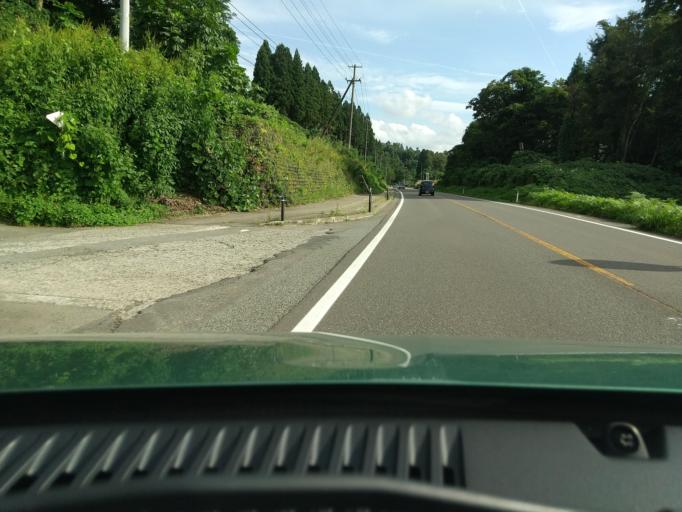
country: JP
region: Akita
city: Yokotemachi
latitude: 39.3408
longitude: 140.5596
